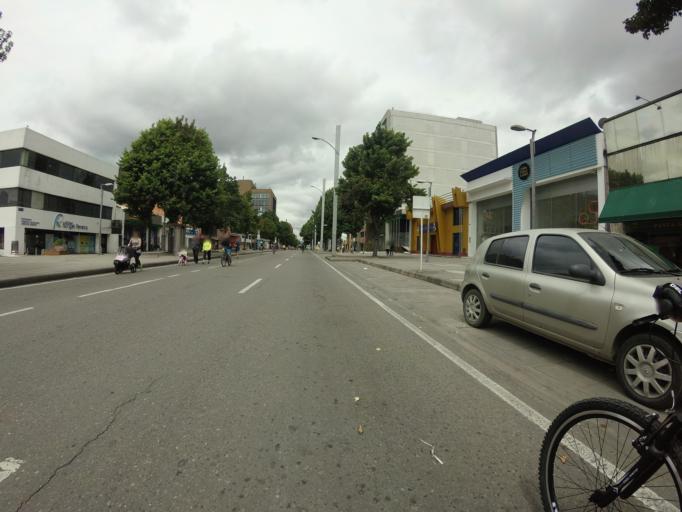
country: CO
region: Bogota D.C.
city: Barrio San Luis
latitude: 4.6820
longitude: -74.0493
